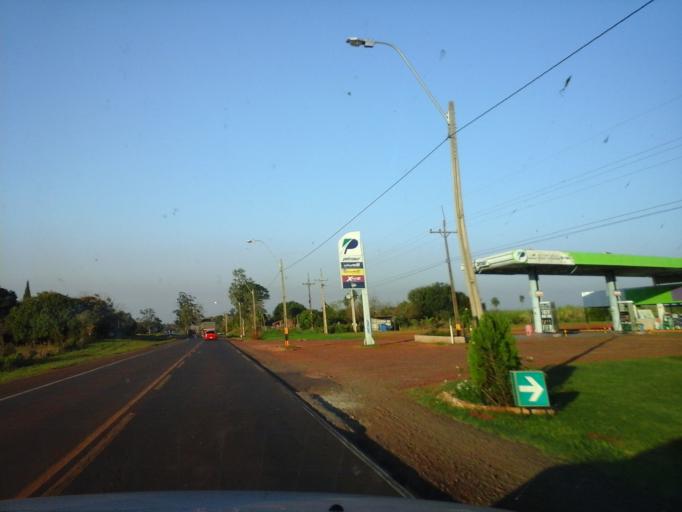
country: PY
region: Itapua
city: General Delgado
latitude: -27.0895
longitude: -56.5099
